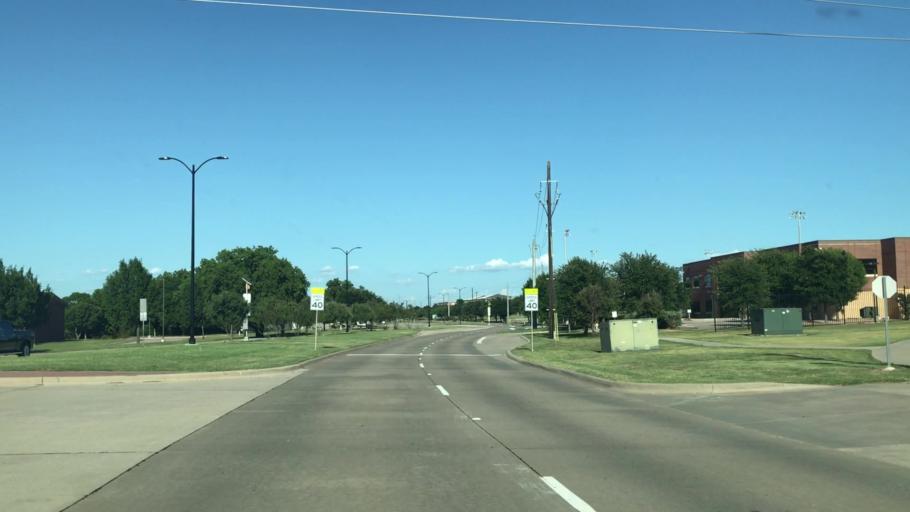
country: US
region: Texas
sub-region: Collin County
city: Frisco
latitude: 33.1380
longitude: -96.7751
